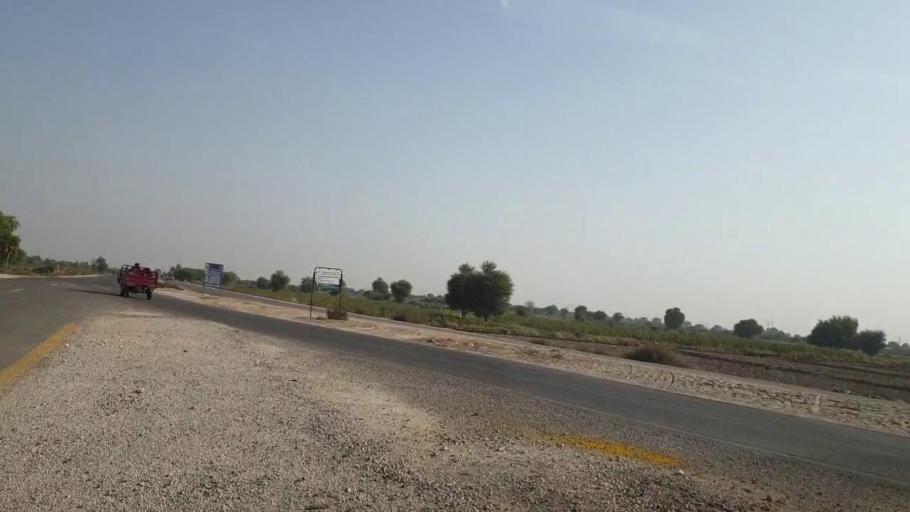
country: PK
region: Sindh
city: Sehwan
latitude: 26.4546
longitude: 67.8088
